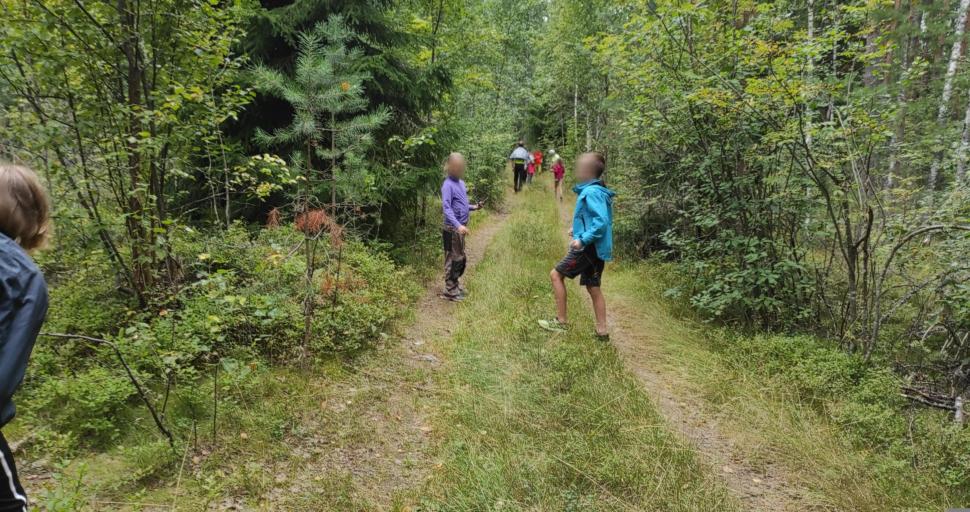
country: RU
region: Leningrad
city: Veshchevo
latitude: 60.6490
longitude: 29.2591
